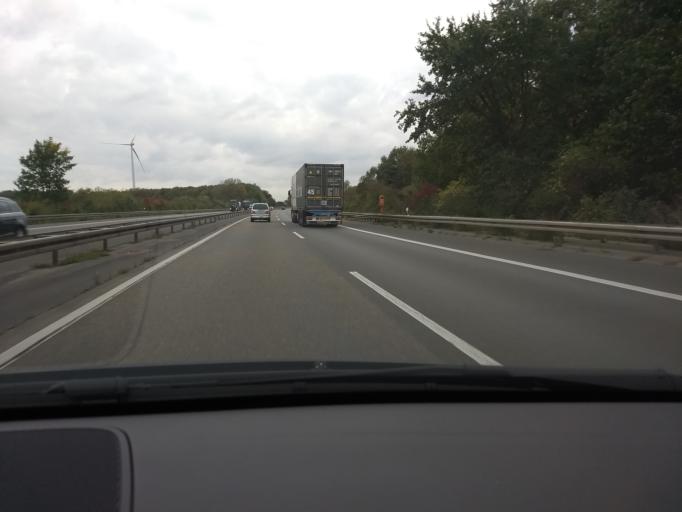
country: DE
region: North Rhine-Westphalia
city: Dorsten
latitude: 51.6694
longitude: 6.9191
